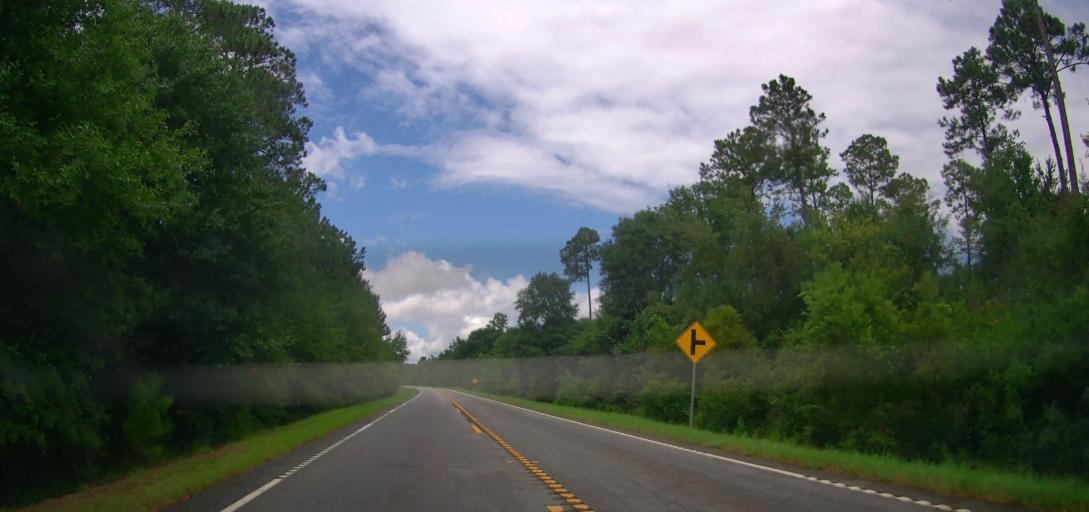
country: US
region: Georgia
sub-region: Crisp County
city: Cordele
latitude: 32.0422
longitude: -83.6185
